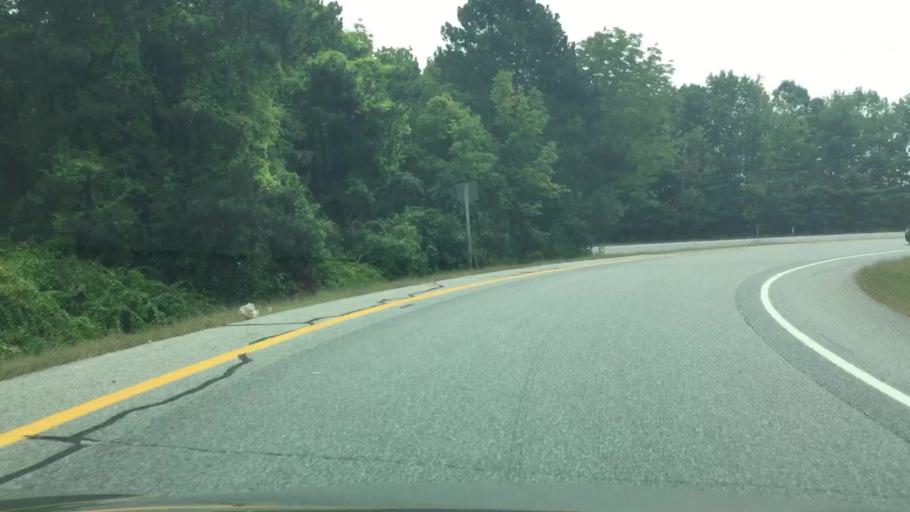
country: US
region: Maine
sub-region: Kennebec County
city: Augusta
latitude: 44.3465
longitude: -69.7915
